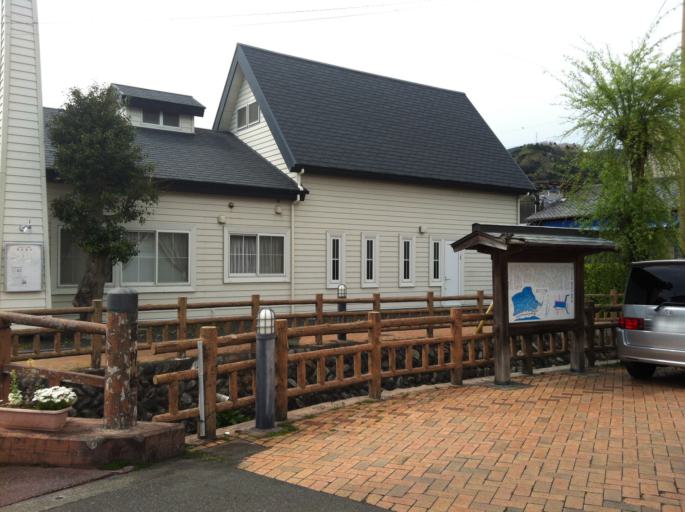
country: JP
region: Shizuoka
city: Fuji
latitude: 35.1175
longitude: 138.6060
